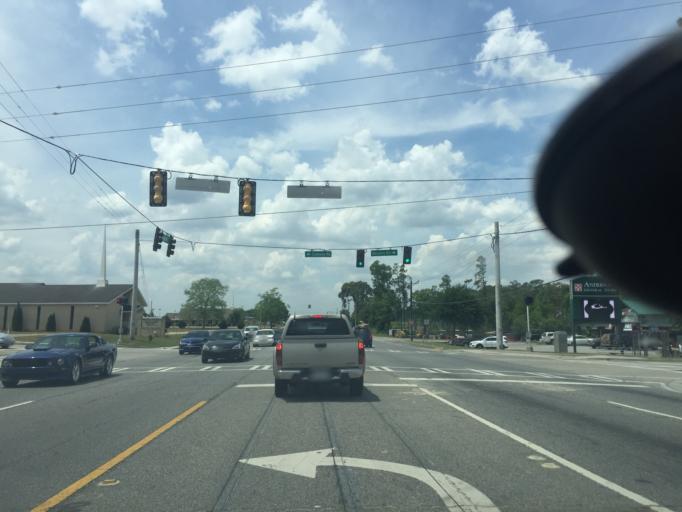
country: US
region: Georgia
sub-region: Bulloch County
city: Statesboro
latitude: 32.4307
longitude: -81.7489
